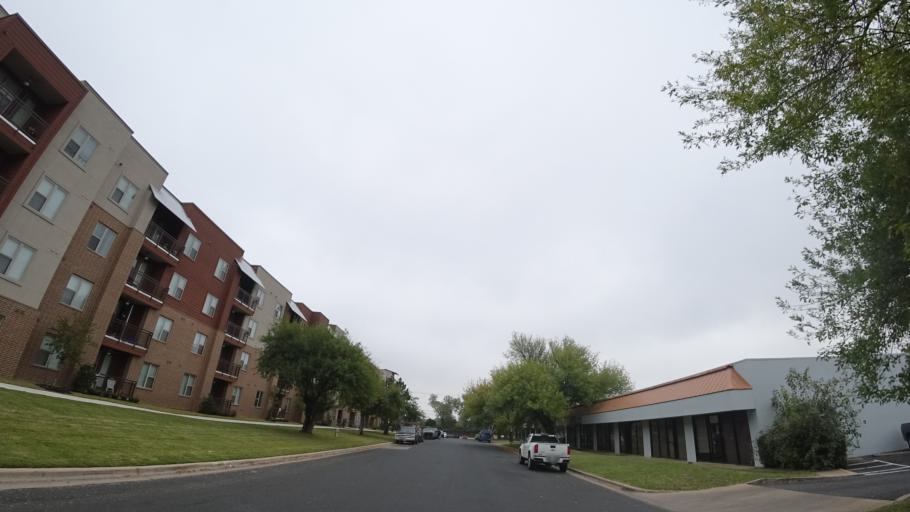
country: US
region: Texas
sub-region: Travis County
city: Austin
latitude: 30.2095
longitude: -97.7741
